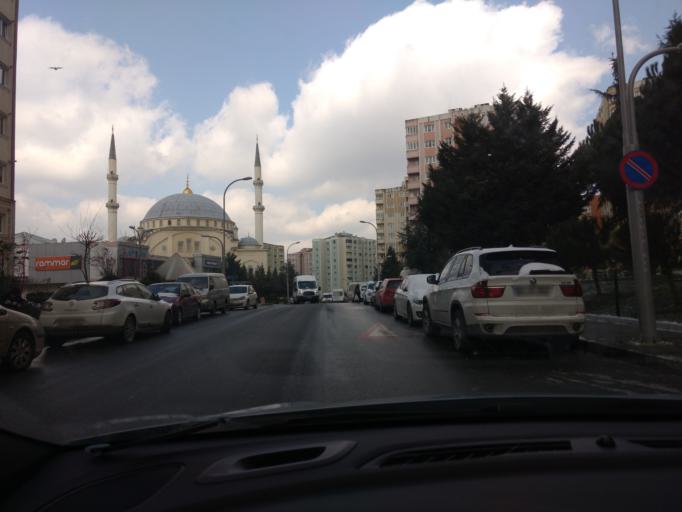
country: TR
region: Istanbul
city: Basaksehir
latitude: 41.1078
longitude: 28.8105
